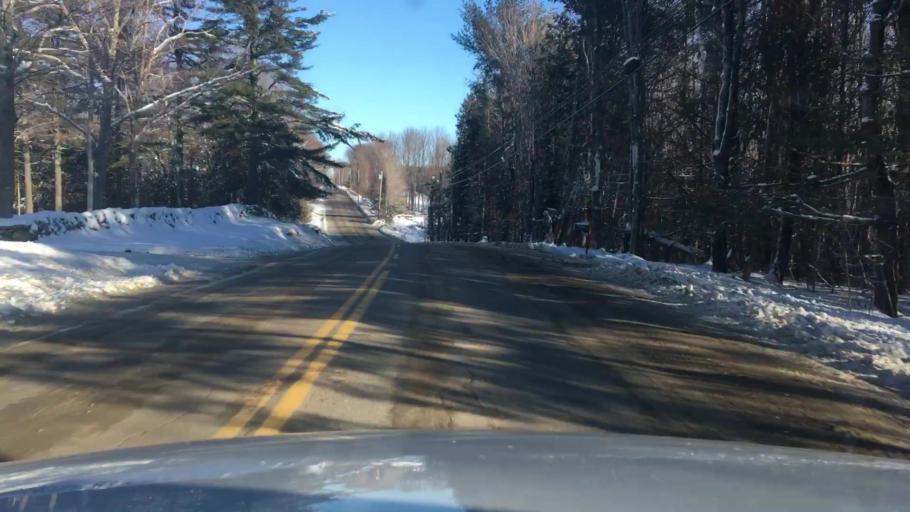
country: US
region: Maine
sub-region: Kennebec County
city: Mount Vernon
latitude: 44.4740
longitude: -69.9728
